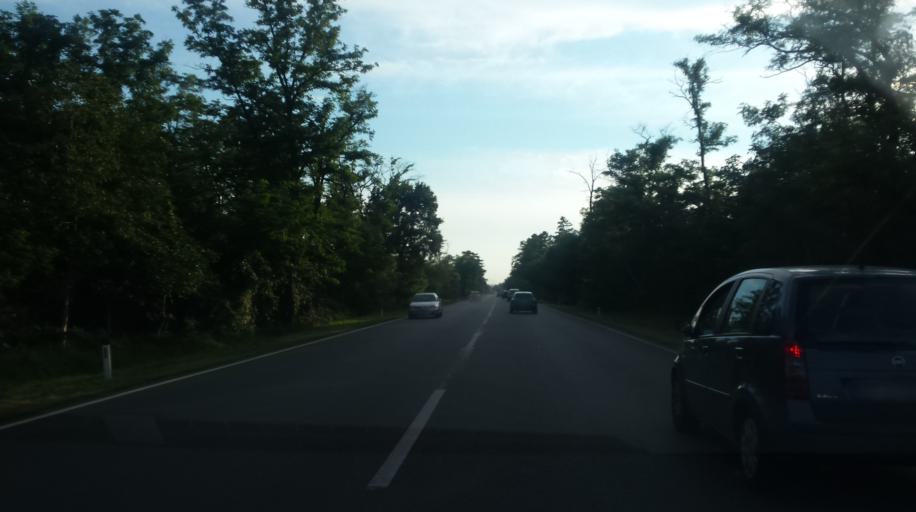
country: AT
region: Lower Austria
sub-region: Politischer Bezirk Ganserndorf
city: Deutsch-Wagram
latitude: 48.3072
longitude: 16.5900
